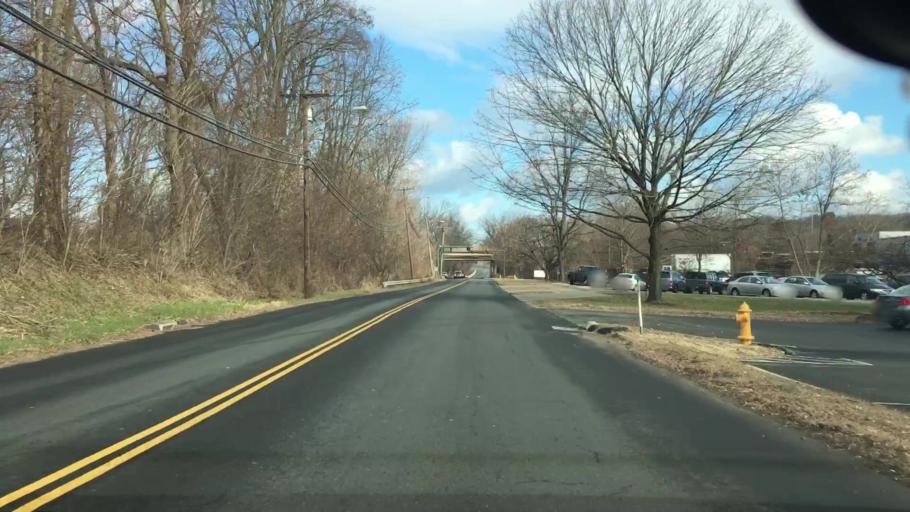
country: US
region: Connecticut
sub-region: Fairfield County
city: Danbury
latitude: 41.4153
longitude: -73.4220
